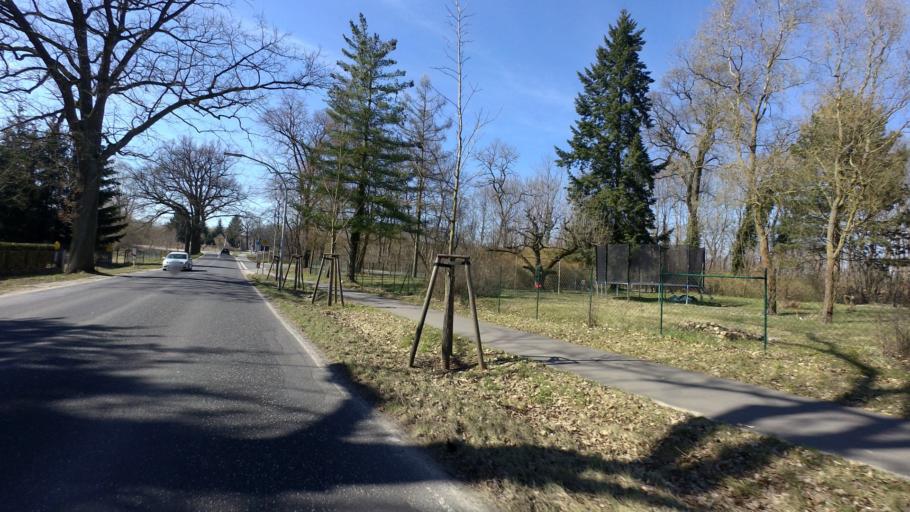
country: DE
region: Brandenburg
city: Waldsieversdorf
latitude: 52.5232
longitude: 14.0975
